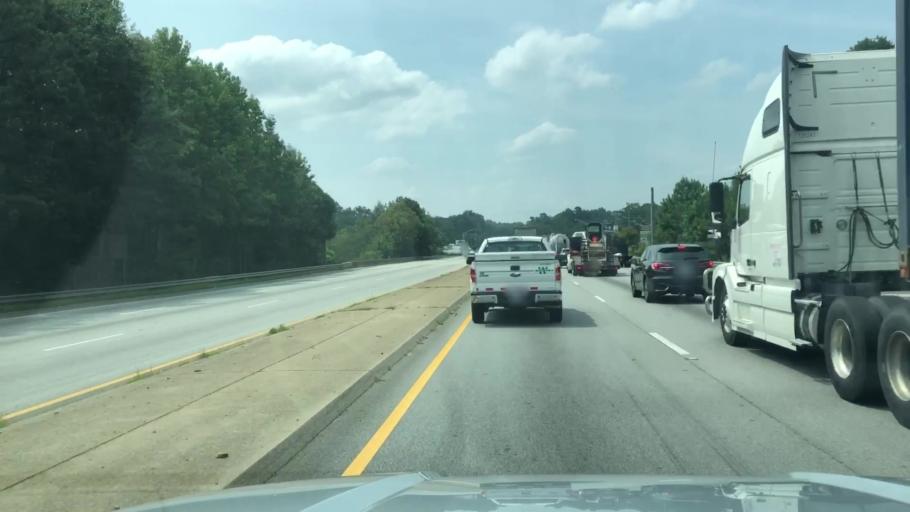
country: US
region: Georgia
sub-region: Cobb County
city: Austell
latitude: 33.7960
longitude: -84.6397
